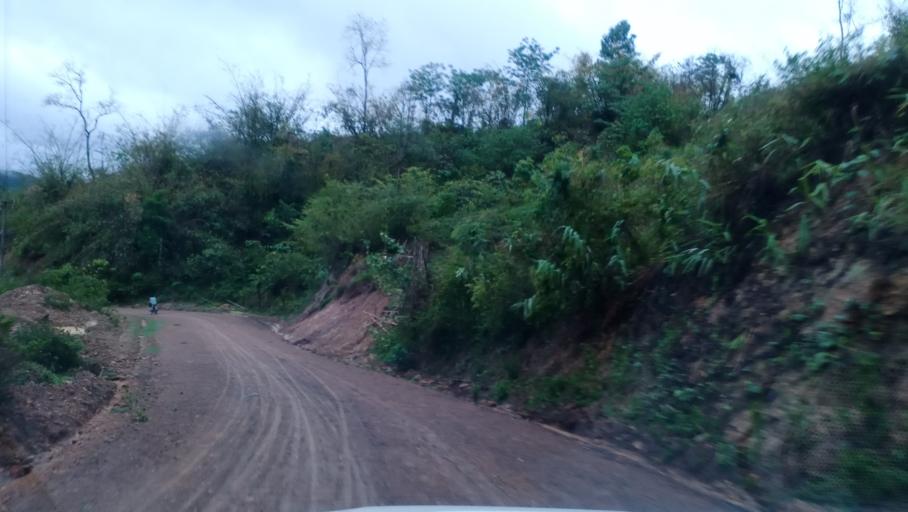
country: VN
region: Huyen Dien Bien
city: Dien Bien Phu
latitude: 21.3282
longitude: 102.7161
